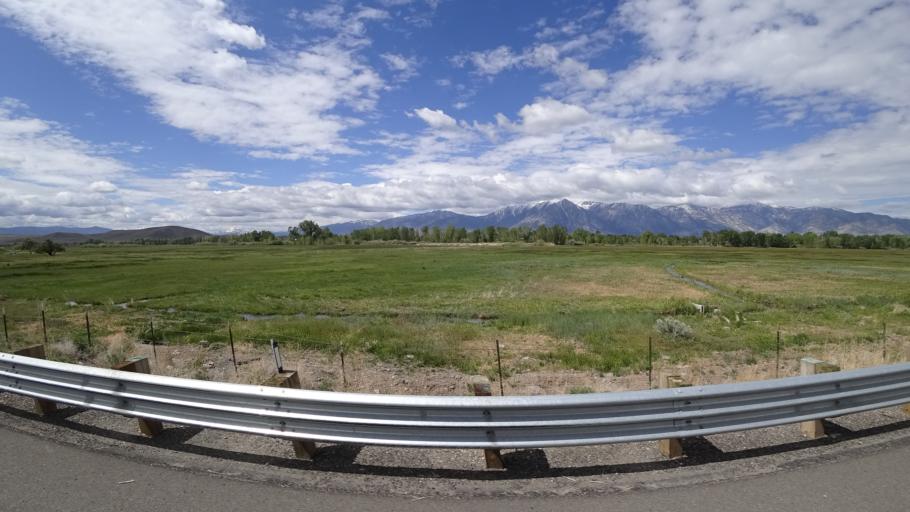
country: US
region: Nevada
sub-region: Douglas County
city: Gardnerville Ranchos
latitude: 38.9086
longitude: -119.7087
